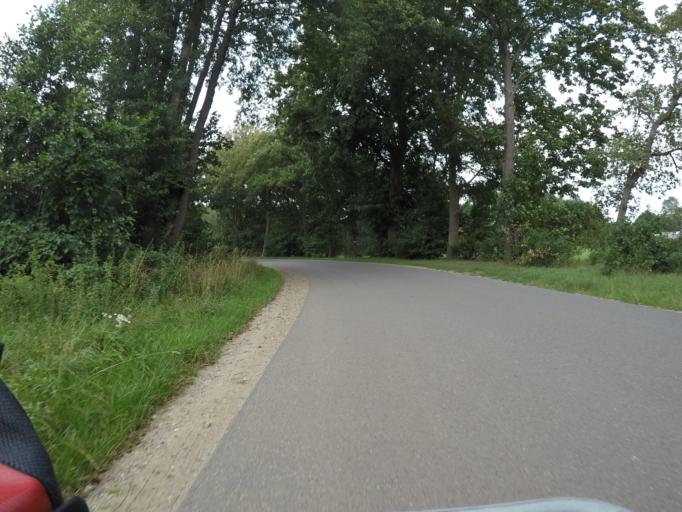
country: DE
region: Lower Saxony
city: Bardowick
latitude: 53.3048
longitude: 10.4038
